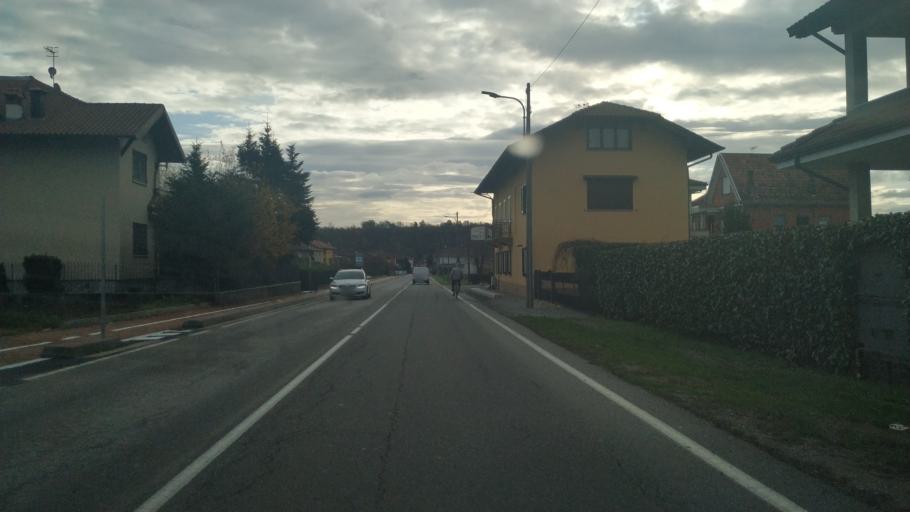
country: IT
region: Piedmont
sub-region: Provincia di Novara
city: Prato Sesia
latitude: 45.6525
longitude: 8.3681
